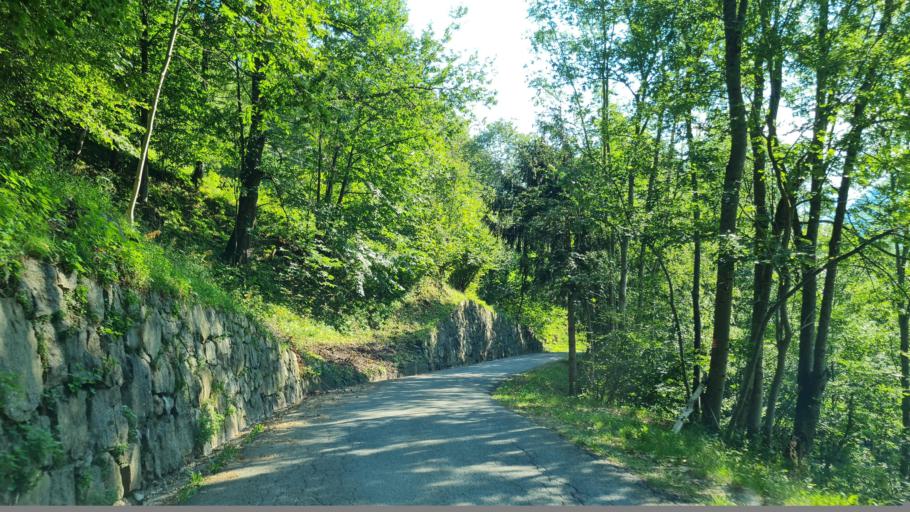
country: IT
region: Aosta Valley
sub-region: Valle d'Aosta
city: Lillianes
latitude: 45.6290
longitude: 7.8500
